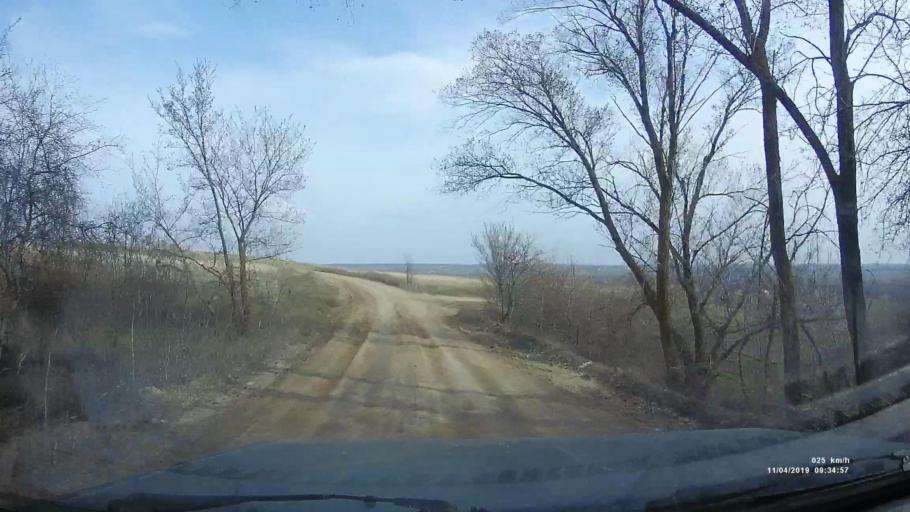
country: RU
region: Rostov
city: Staraya Stanitsa
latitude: 48.2705
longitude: 40.3716
